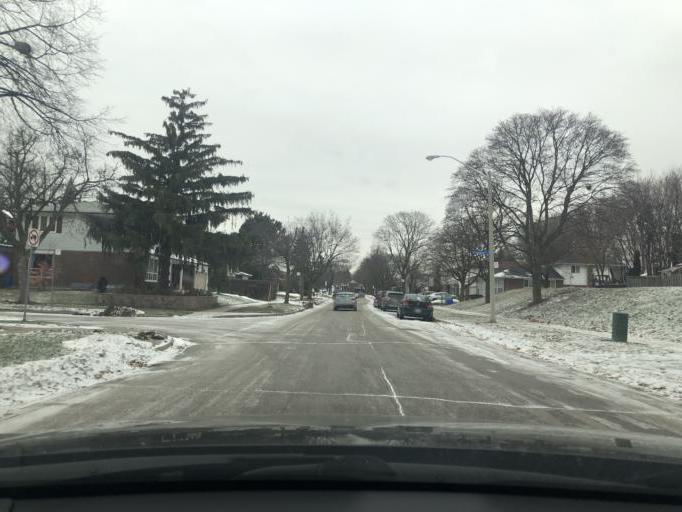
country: CA
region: Ontario
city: Scarborough
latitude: 43.7828
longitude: -79.3038
